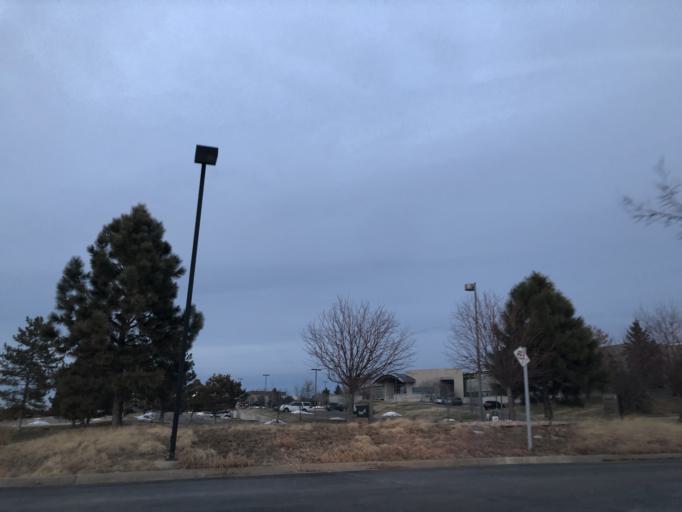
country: US
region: Colorado
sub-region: Douglas County
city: Meridian
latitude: 39.5593
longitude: -104.8609
